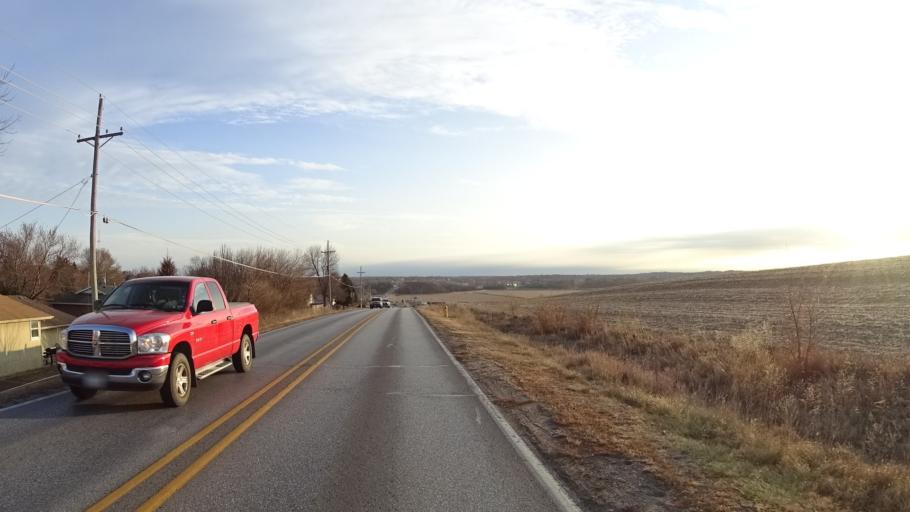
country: US
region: Nebraska
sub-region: Sarpy County
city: Offutt Air Force Base
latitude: 41.1653
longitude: -95.9672
